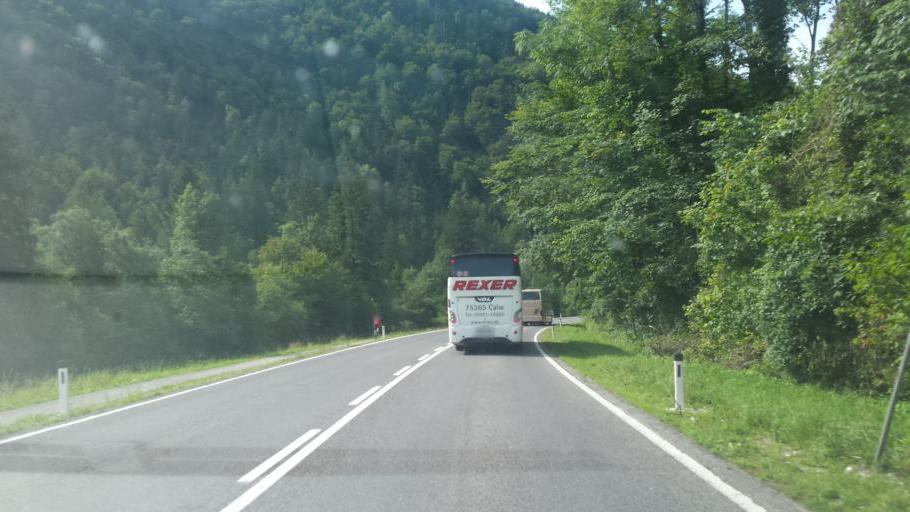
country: AT
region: Upper Austria
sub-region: Politischer Bezirk Gmunden
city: Bad Ischl
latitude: 47.7314
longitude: 13.6592
